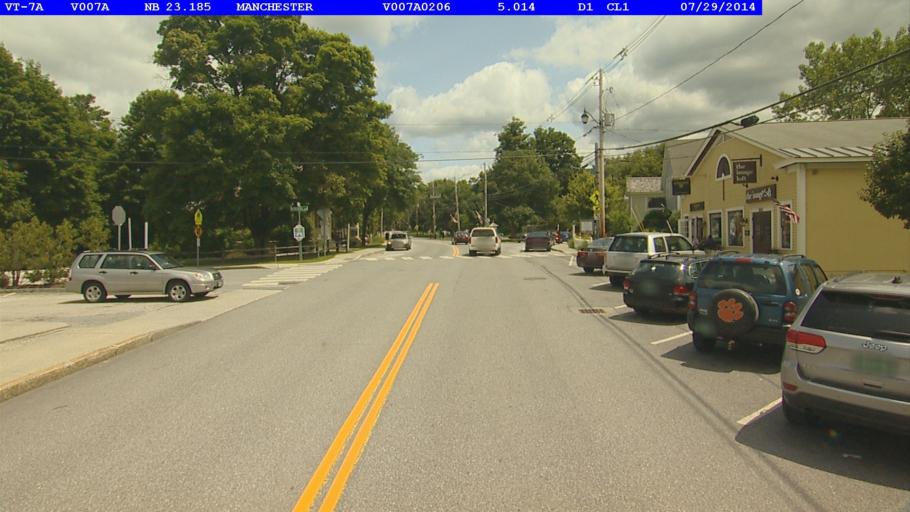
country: US
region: Vermont
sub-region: Bennington County
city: Manchester Center
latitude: 43.1775
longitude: -73.0543
